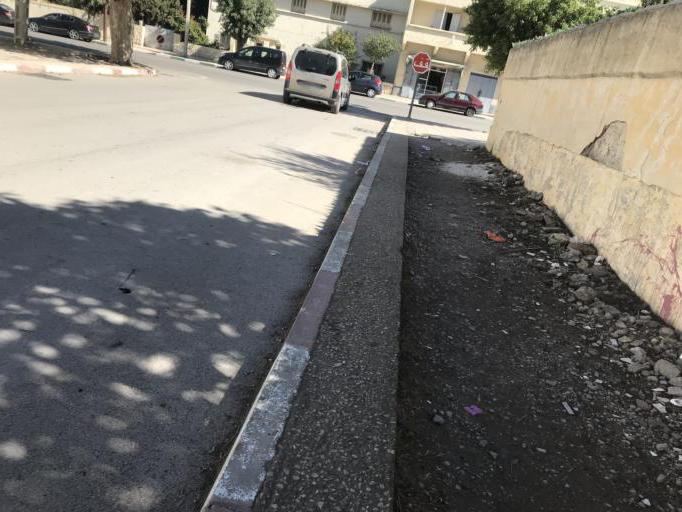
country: MA
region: Taza-Al Hoceima-Taounate
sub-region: Taza
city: Taza
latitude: 34.2186
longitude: -4.0062
